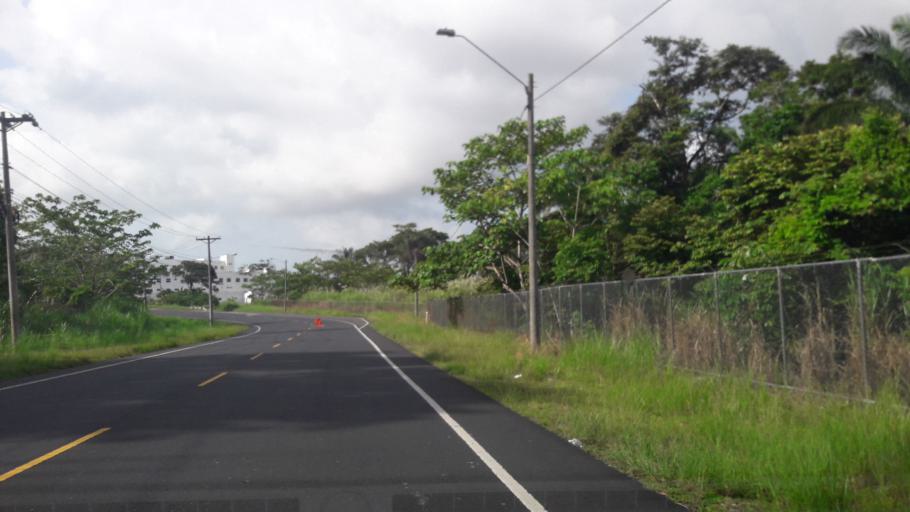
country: PA
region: Colon
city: Cativa
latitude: 9.3551
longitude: -79.8628
